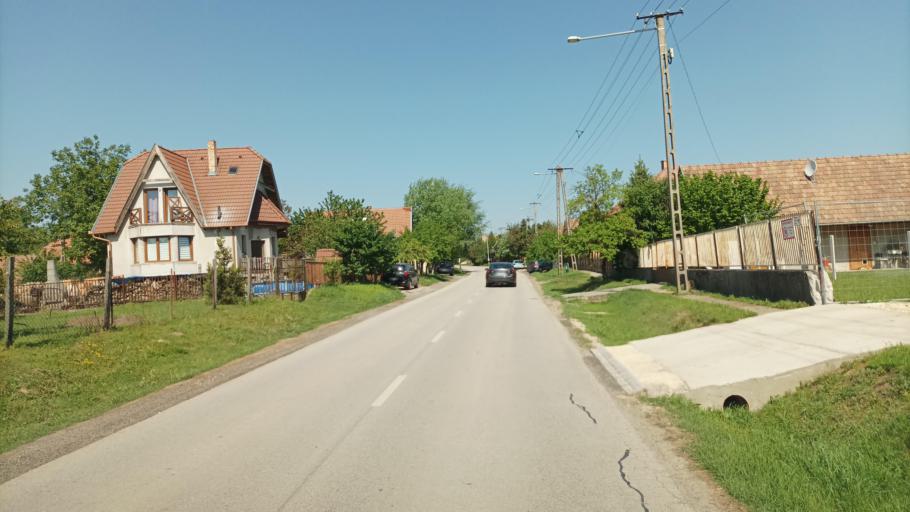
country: HU
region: Pest
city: Gomba
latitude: 47.3735
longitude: 19.5236
